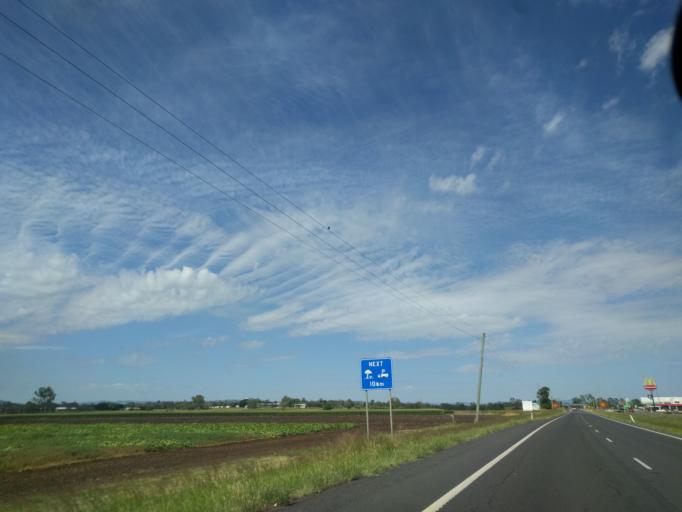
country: AU
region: Queensland
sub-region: Lockyer Valley
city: Gatton
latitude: -27.5444
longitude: 152.3492
